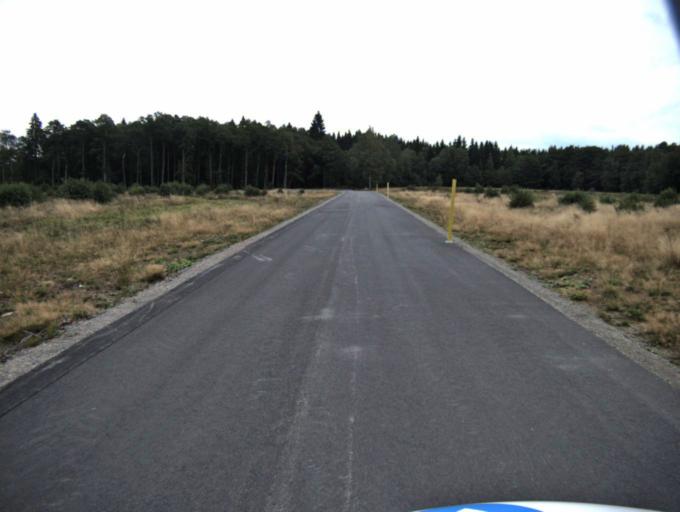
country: SE
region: Vaestra Goetaland
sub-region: Ulricehamns Kommun
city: Ulricehamn
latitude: 57.8027
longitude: 13.4492
